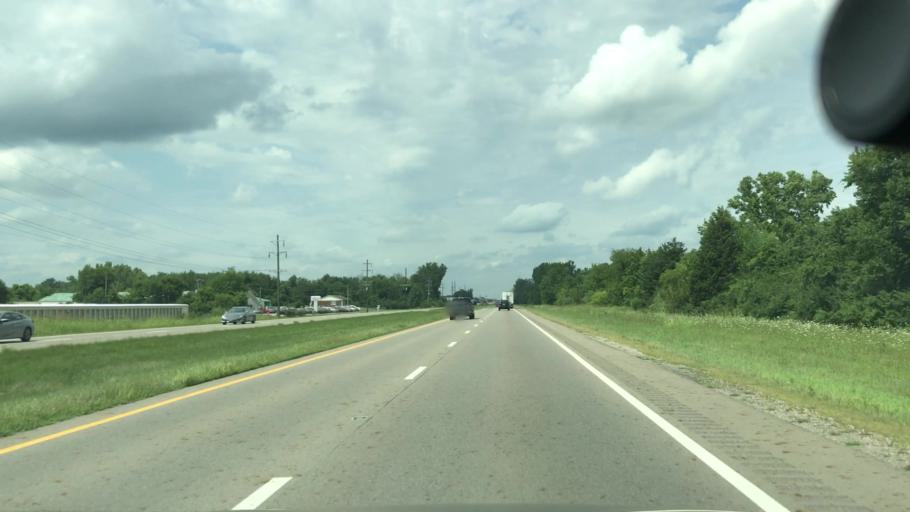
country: US
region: Ohio
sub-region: Pickaway County
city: Circleville
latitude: 39.6351
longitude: -82.9556
